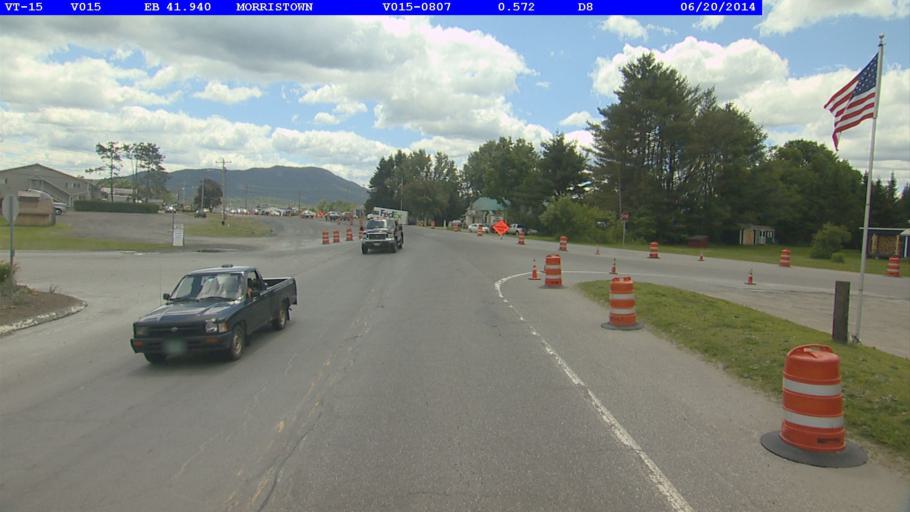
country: US
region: Vermont
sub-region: Lamoille County
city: Morrisville
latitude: 44.5786
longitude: -72.5968
